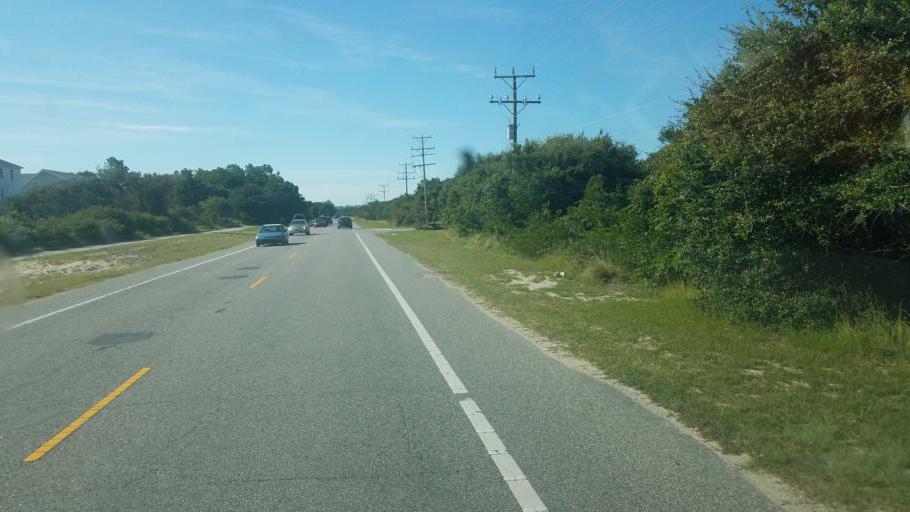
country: US
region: North Carolina
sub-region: Dare County
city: Southern Shores
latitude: 36.3223
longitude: -75.8161
